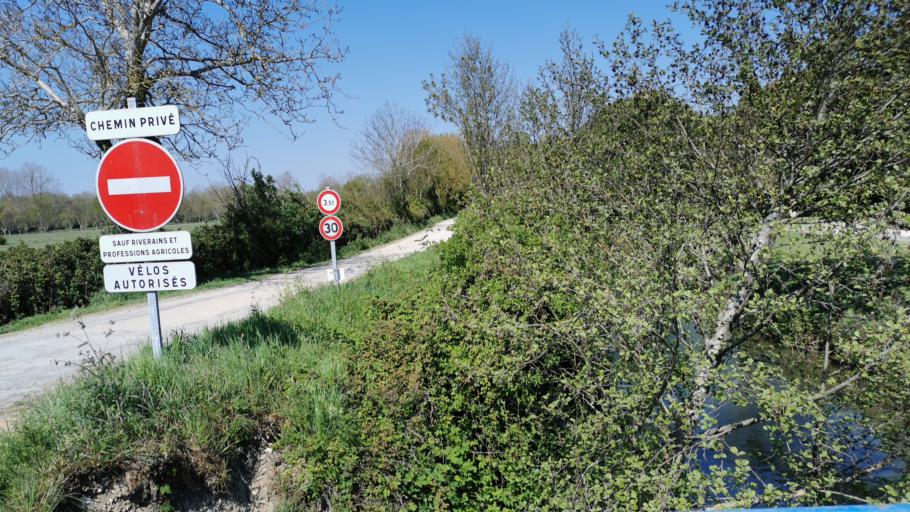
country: FR
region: Poitou-Charentes
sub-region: Departement des Deux-Sevres
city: Coulon
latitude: 46.3215
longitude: -0.6249
